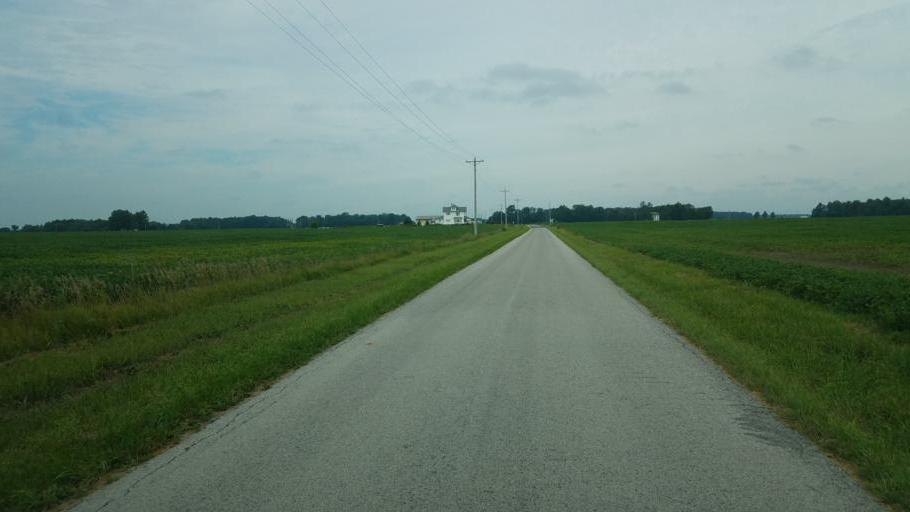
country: US
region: Ohio
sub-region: Morrow County
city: Cardington
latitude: 40.4997
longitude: -82.9549
